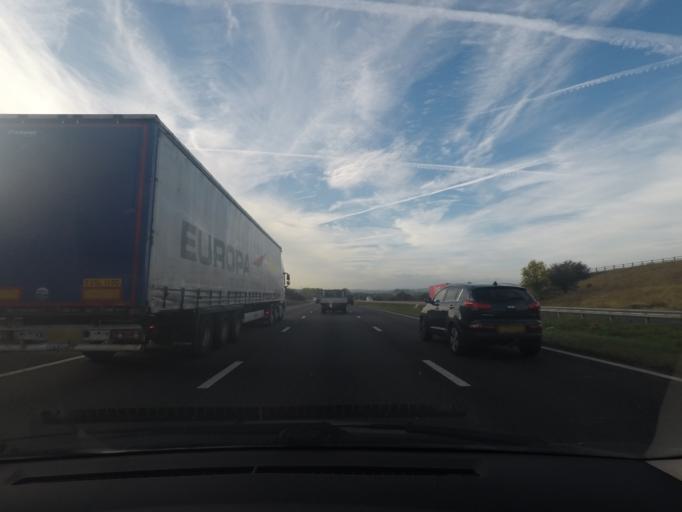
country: GB
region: England
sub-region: Barnsley
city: Darton
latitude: 53.5793
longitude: -1.5377
